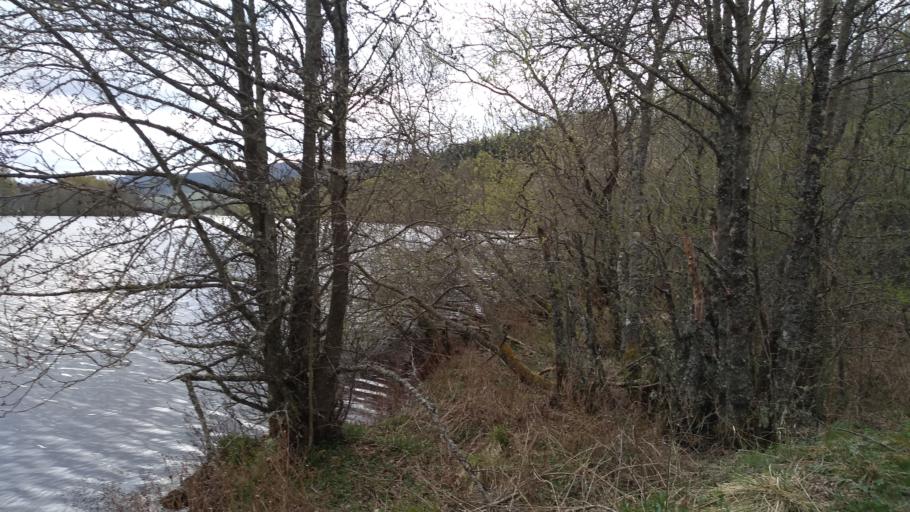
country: GB
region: Scotland
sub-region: Perth and Kinross
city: Aberfeldy
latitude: 56.7057
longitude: -4.0033
